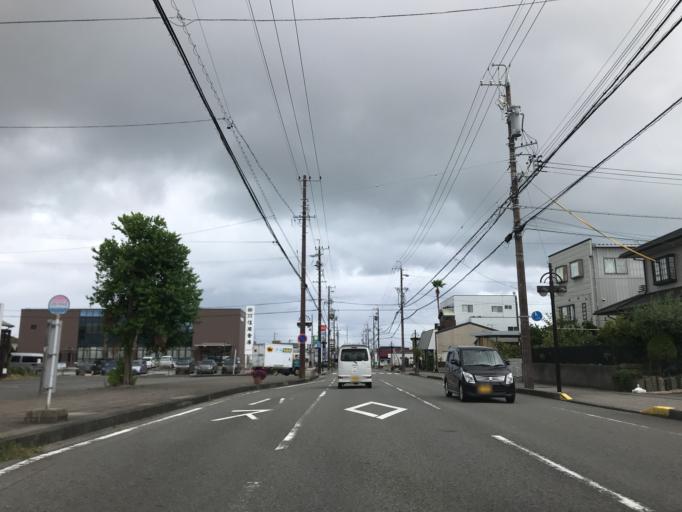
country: JP
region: Shizuoka
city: Sagara
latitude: 34.6435
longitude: 138.1279
